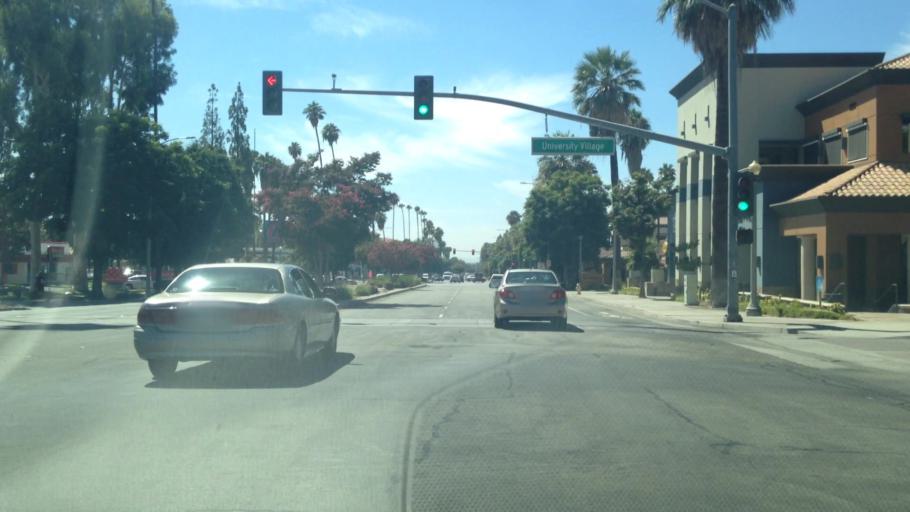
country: US
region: California
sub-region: Riverside County
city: Highgrove
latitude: 33.9758
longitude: -117.3377
